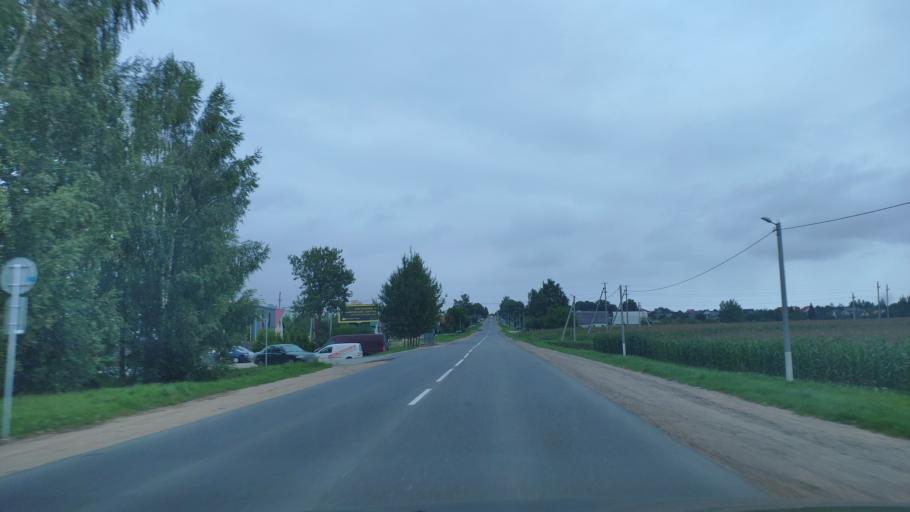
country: BY
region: Minsk
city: Azyartso
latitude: 53.8388
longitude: 27.3775
